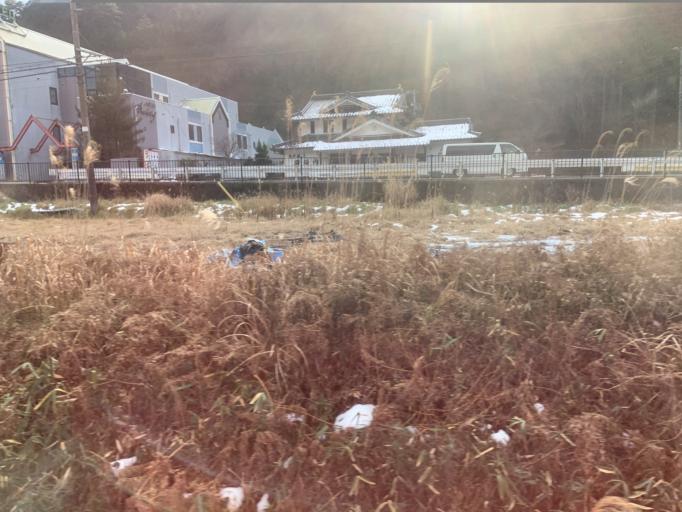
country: JP
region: Gifu
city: Takayama
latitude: 35.9272
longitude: 137.2289
